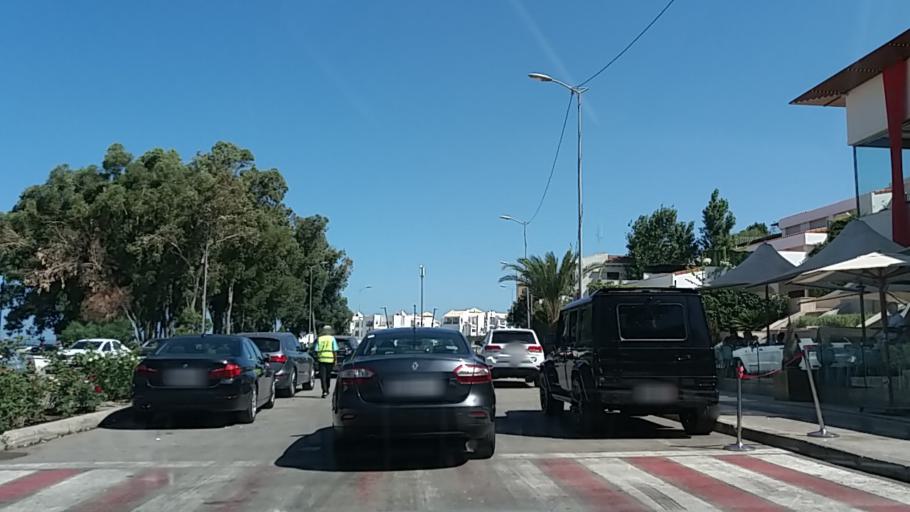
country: MA
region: Tanger-Tetouan
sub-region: Tanger-Assilah
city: Tangier
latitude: 35.7837
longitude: -5.7615
